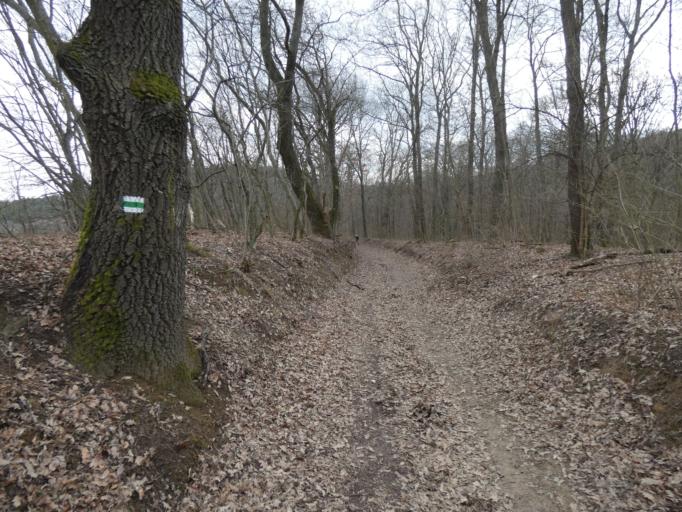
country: HU
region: Pest
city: Pilisborosjeno
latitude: 47.6218
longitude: 19.0043
